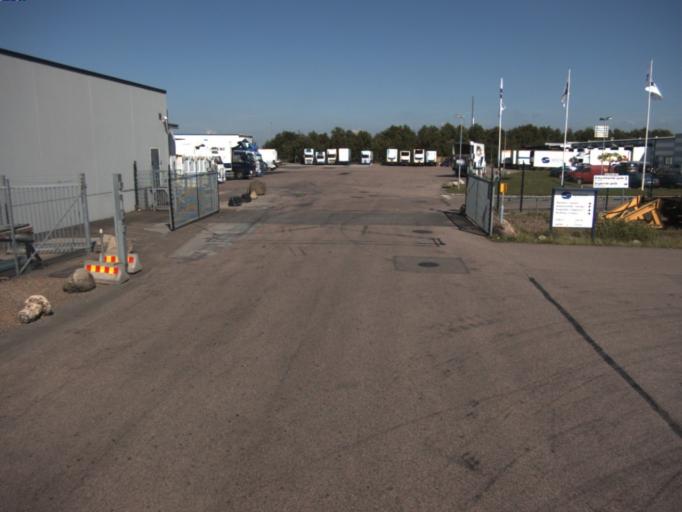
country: SE
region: Skane
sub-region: Helsingborg
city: Barslov
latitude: 56.0443
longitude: 12.7823
